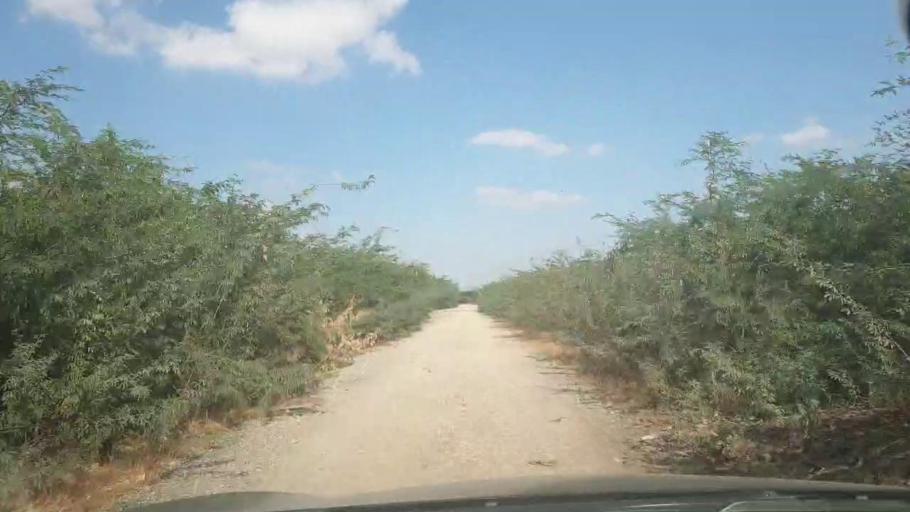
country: PK
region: Sindh
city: Malir Cantonment
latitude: 25.0617
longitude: 67.3960
